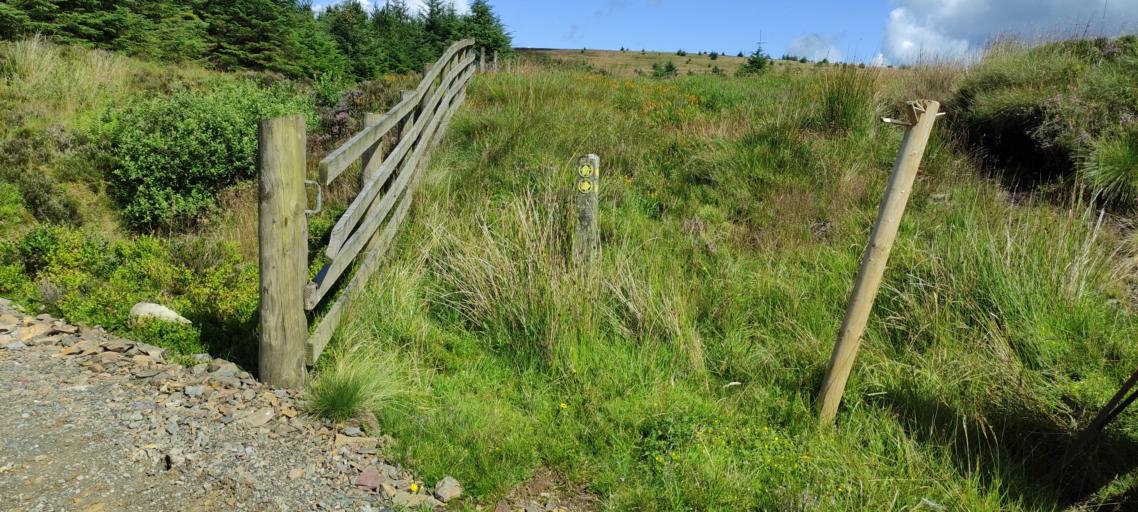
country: GB
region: Scotland
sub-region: Dumfries and Galloway
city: Langholm
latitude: 55.2427
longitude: -3.0356
